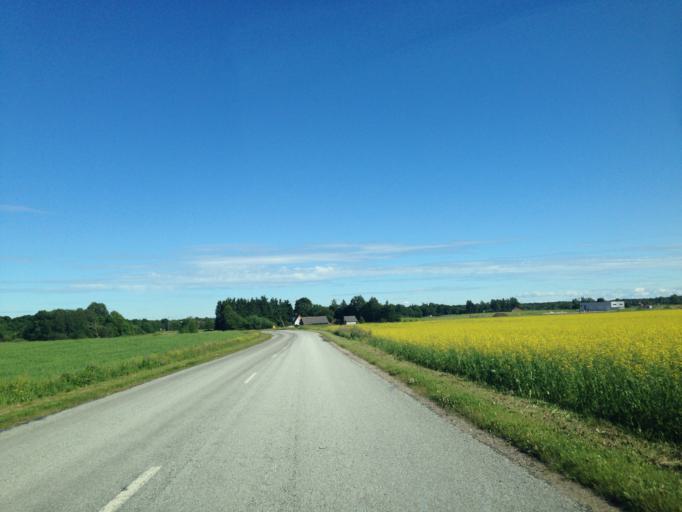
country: EE
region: Harju
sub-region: Kuusalu vald
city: Kuusalu
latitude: 59.4530
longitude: 25.3693
